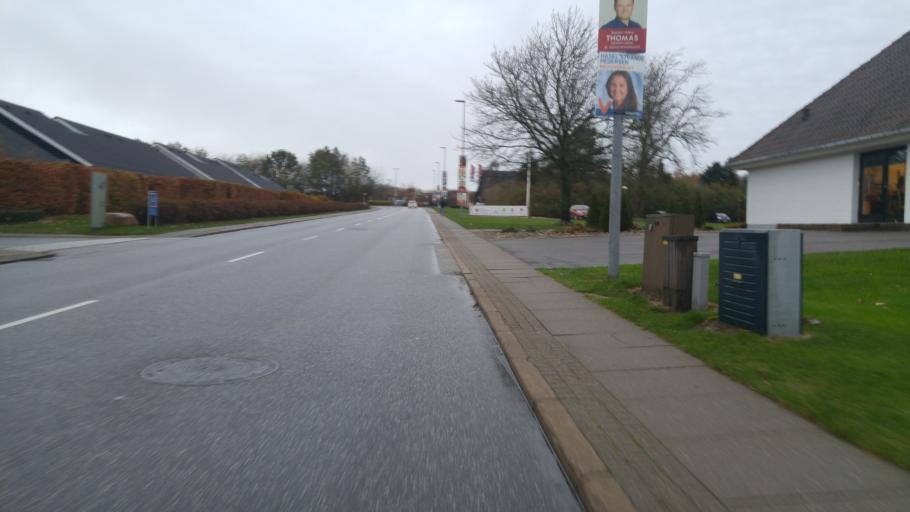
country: DK
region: North Denmark
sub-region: Alborg Kommune
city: Aalborg
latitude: 57.0224
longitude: 9.8874
